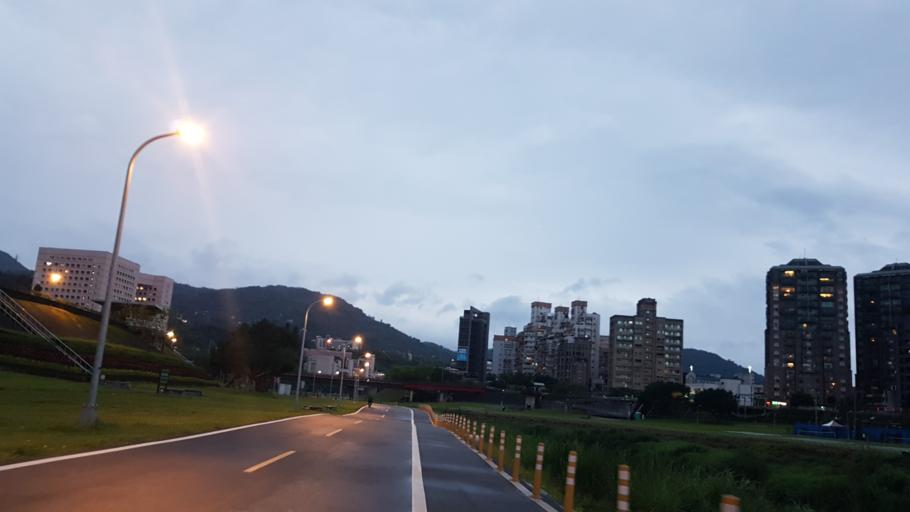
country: TW
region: Taipei
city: Taipei
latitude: 24.9905
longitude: 121.5721
